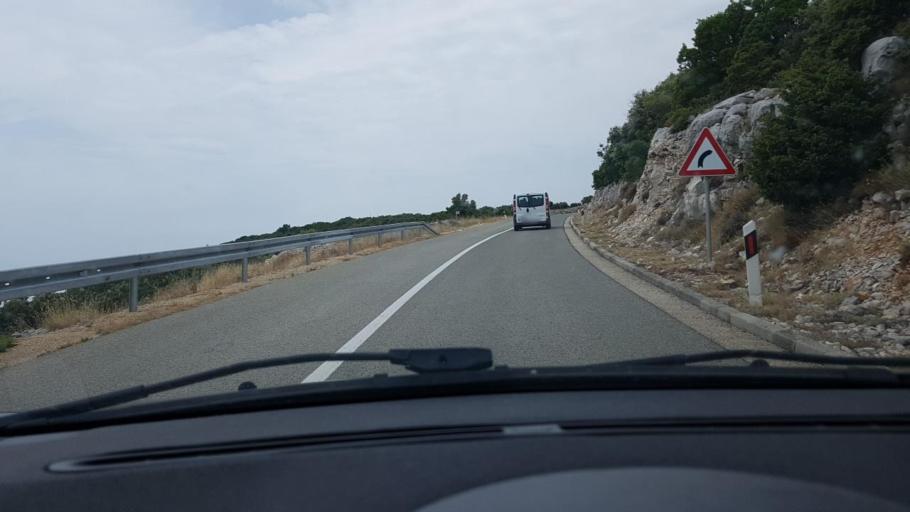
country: HR
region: Dubrovacko-Neretvanska
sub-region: Grad Korcula
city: Zrnovo
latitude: 42.9389
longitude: 17.0099
